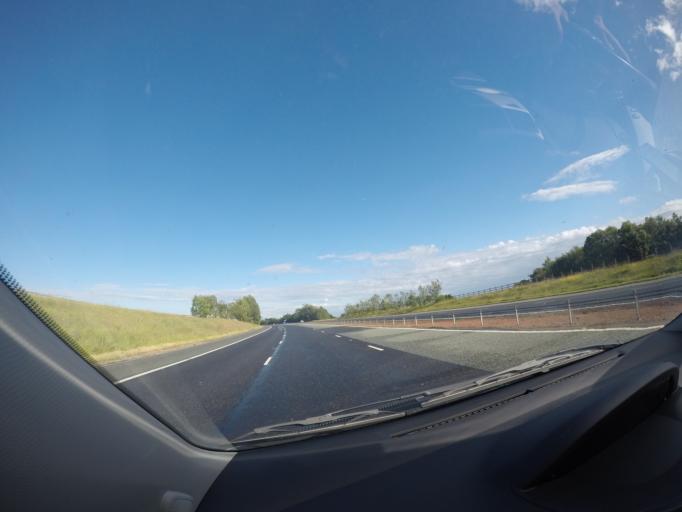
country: GB
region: Scotland
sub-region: Dumfries and Galloway
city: Annan
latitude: 55.0336
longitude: -3.1698
